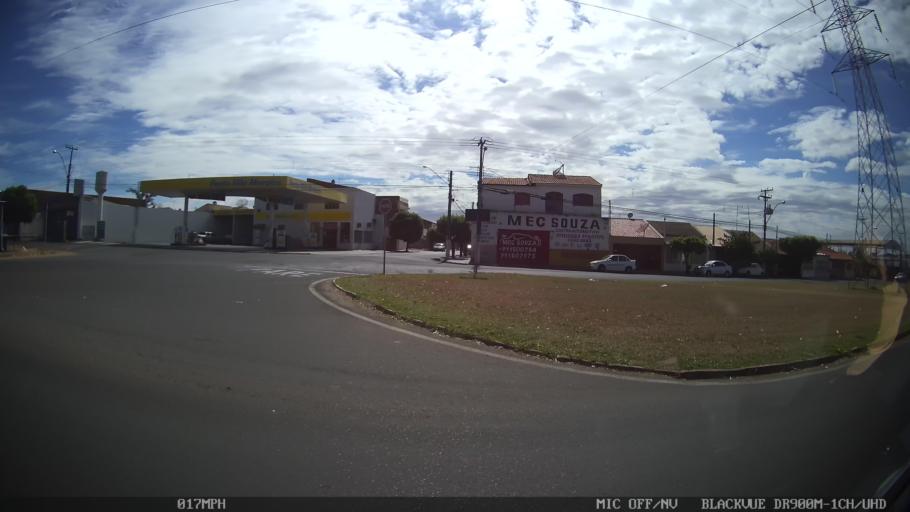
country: BR
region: Sao Paulo
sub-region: Bady Bassitt
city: Bady Bassitt
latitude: -20.8123
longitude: -49.5174
